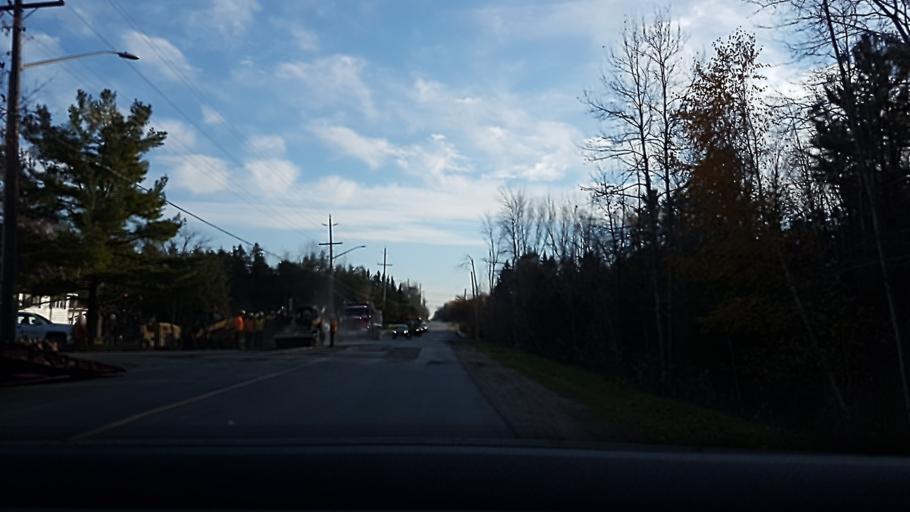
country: CA
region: Ontario
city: Innisfil
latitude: 44.3607
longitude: -79.5509
